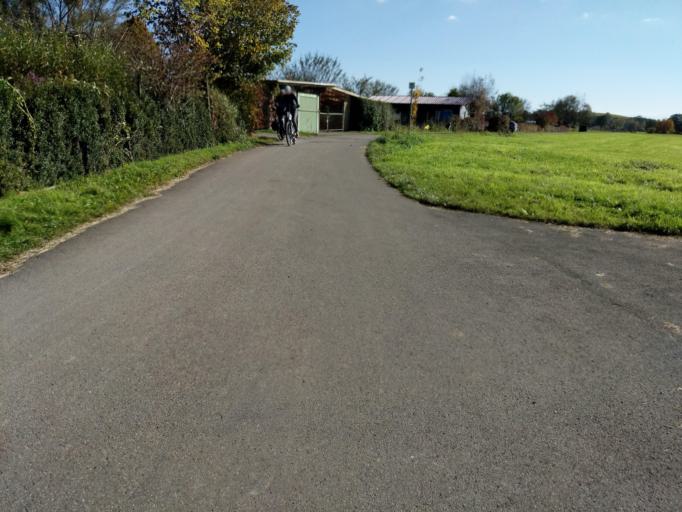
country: DE
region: Baden-Wuerttemberg
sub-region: Tuebingen Region
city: Salem
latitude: 47.7569
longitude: 9.2940
